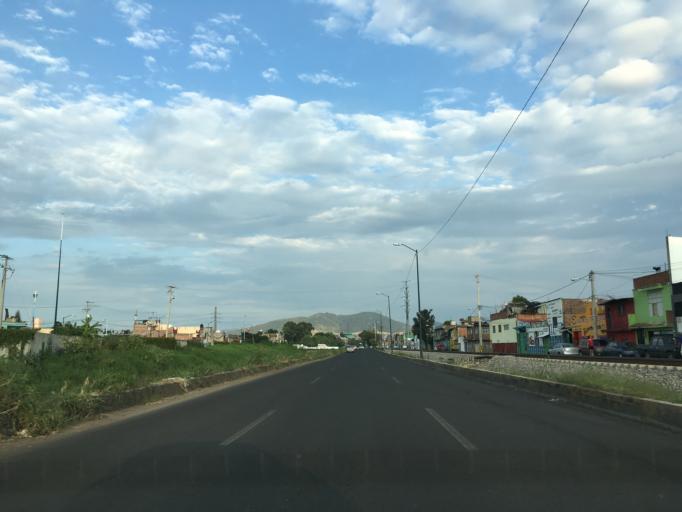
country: MX
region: Michoacan
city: Morelia
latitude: 19.7137
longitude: -101.1999
